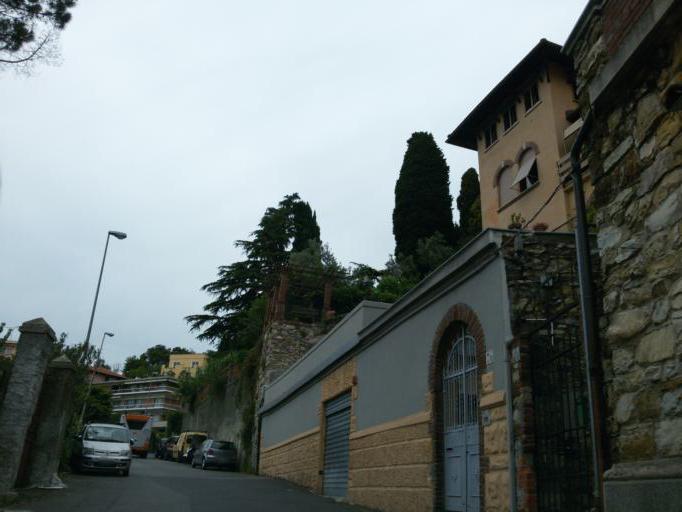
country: IT
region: Liguria
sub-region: Provincia di Genova
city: Genoa
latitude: 44.4213
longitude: 8.9379
